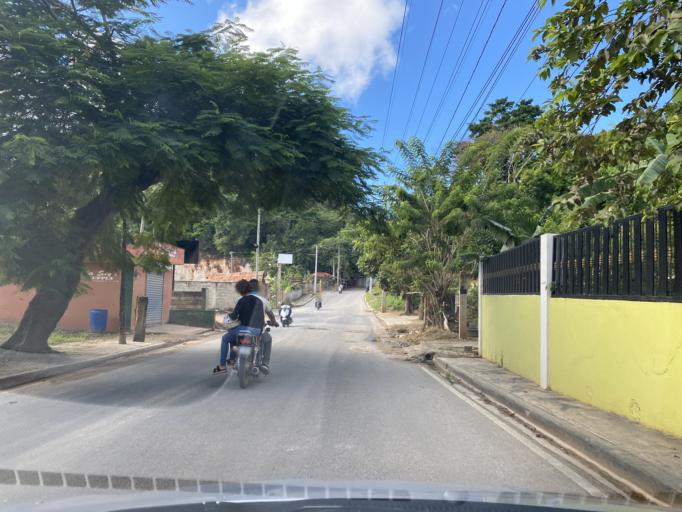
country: DO
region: Samana
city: Las Terrenas
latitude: 19.2971
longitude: -69.5515
